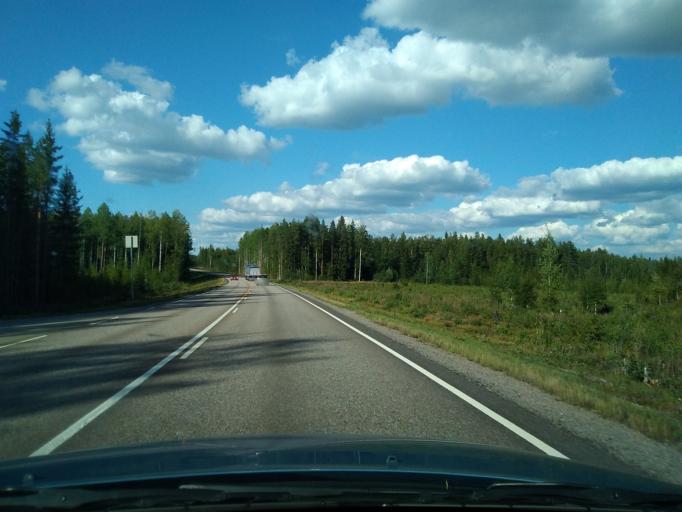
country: FI
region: Pirkanmaa
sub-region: Ylae-Pirkanmaa
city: Maenttae
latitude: 62.1045
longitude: 24.7375
